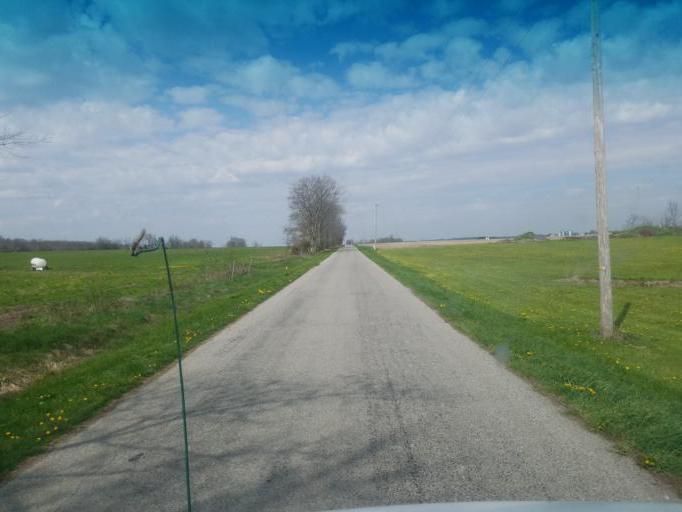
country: US
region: Ohio
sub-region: Logan County
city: Northwood
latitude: 40.4901
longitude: -83.7427
